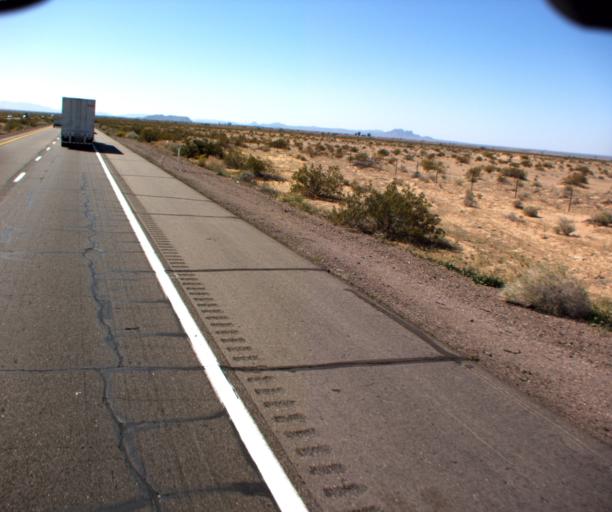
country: US
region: Arizona
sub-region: Yuma County
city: Wellton
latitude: 32.7120
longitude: -113.8329
